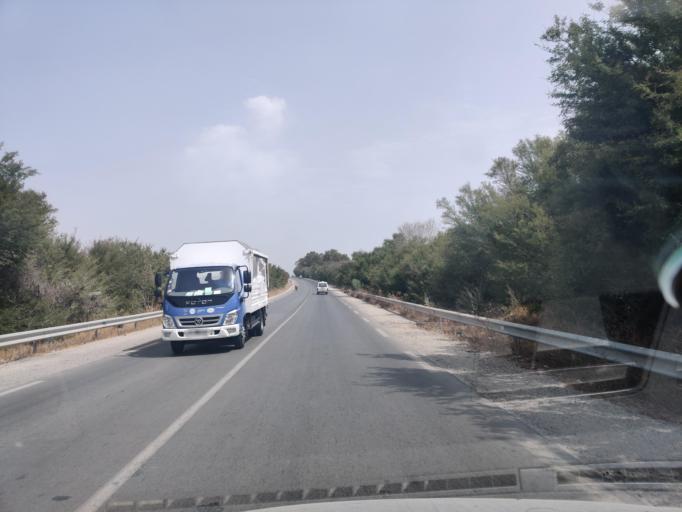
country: TN
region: Nabul
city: Bu `Urqub
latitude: 36.4750
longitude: 10.5722
